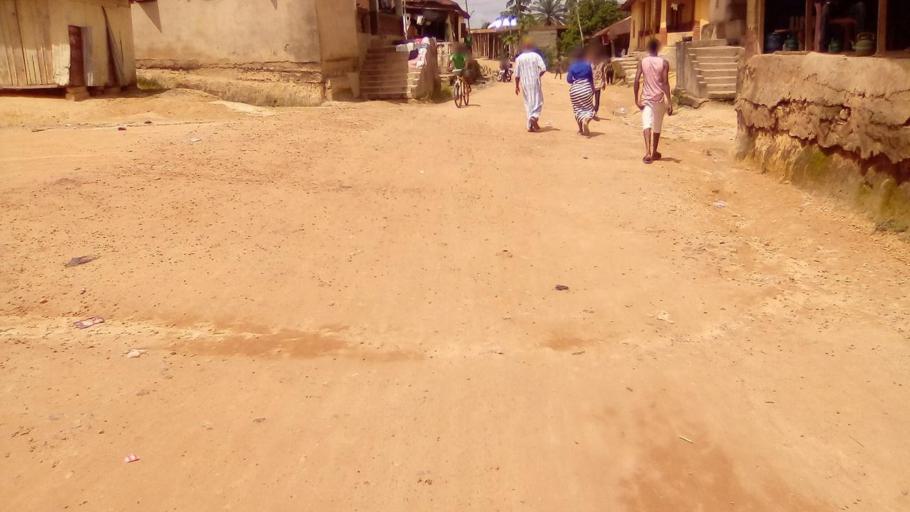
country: SL
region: Southern Province
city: Bo
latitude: 7.9658
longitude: -11.7350
